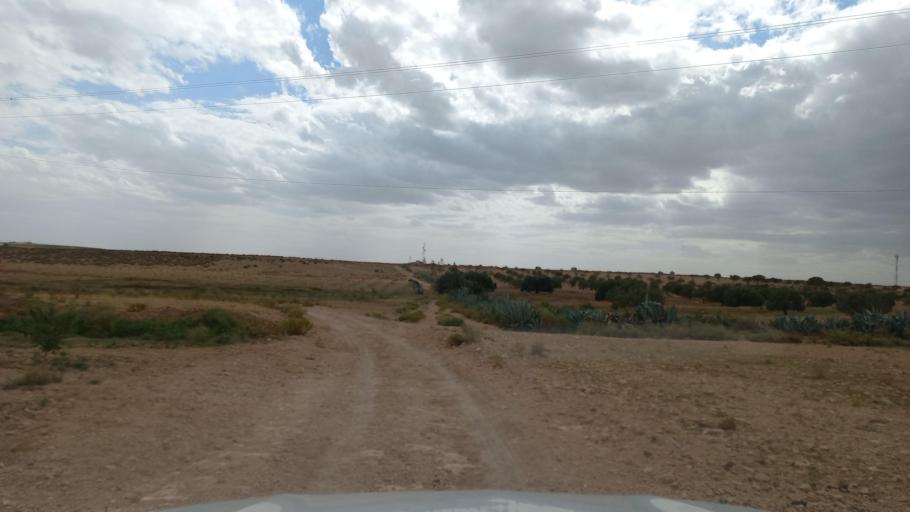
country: TN
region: Al Qasrayn
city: Sbiba
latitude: 35.3844
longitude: 9.1045
